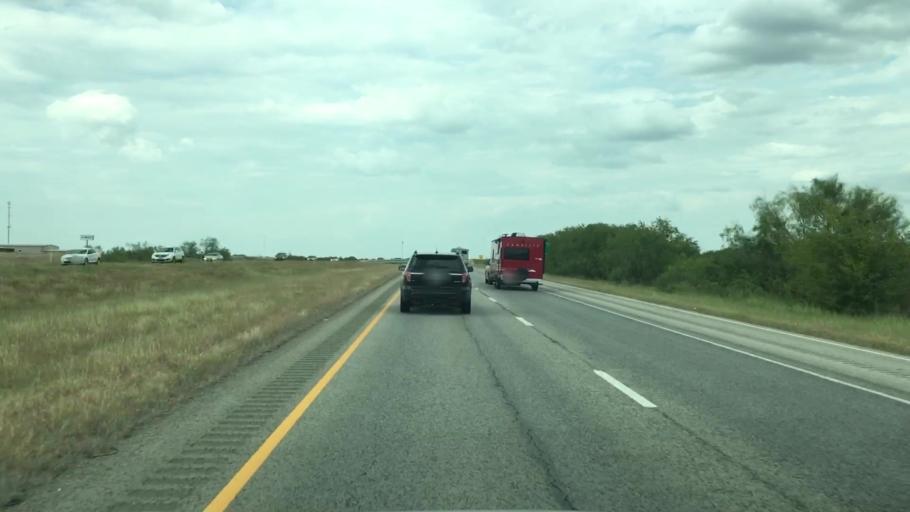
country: US
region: Texas
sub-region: Atascosa County
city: Pleasanton
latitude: 29.0996
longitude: -98.4325
